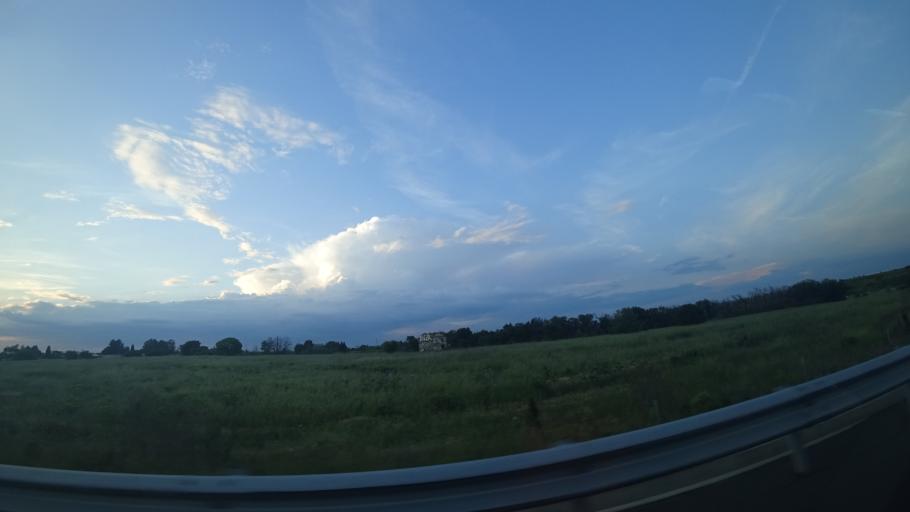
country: FR
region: Languedoc-Roussillon
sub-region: Departement de l'Herault
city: Boujan-sur-Libron
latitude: 43.3582
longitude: 3.2702
